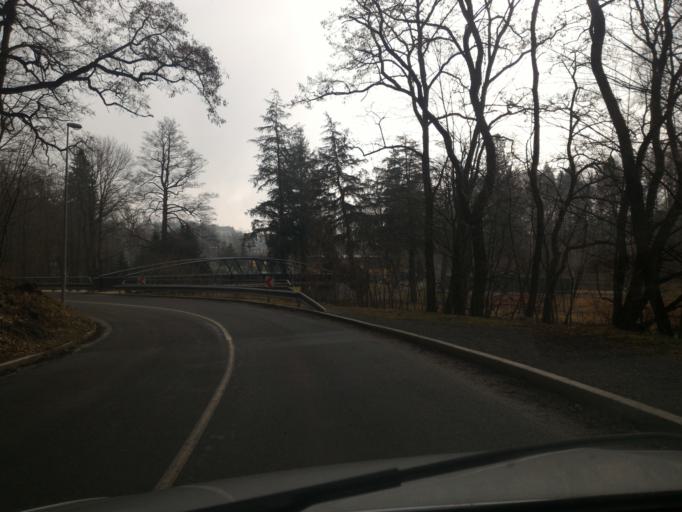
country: CZ
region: Liberecky
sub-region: Okres Liberec
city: Frydlant
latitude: 50.9137
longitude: 15.0825
